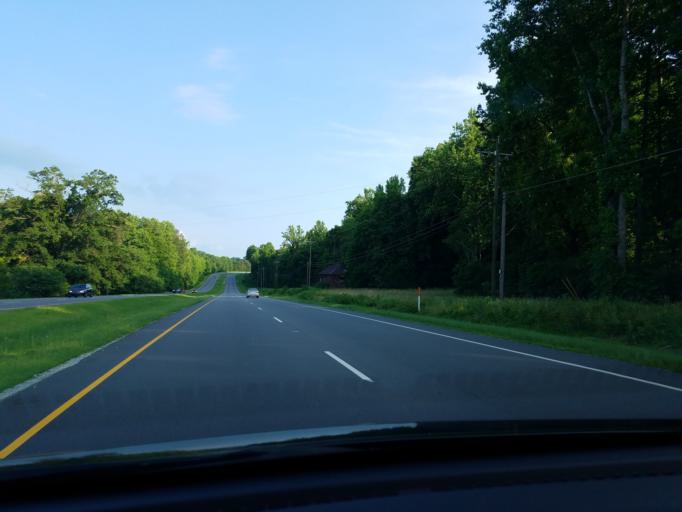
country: US
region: North Carolina
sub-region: Durham County
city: Gorman
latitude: 36.1327
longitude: -78.9045
